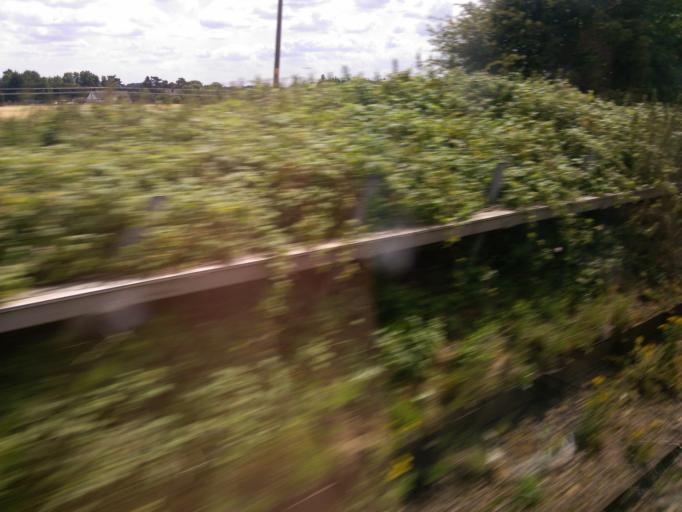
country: GB
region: England
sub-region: Essex
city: Kelvedon
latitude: 51.8532
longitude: 0.7269
